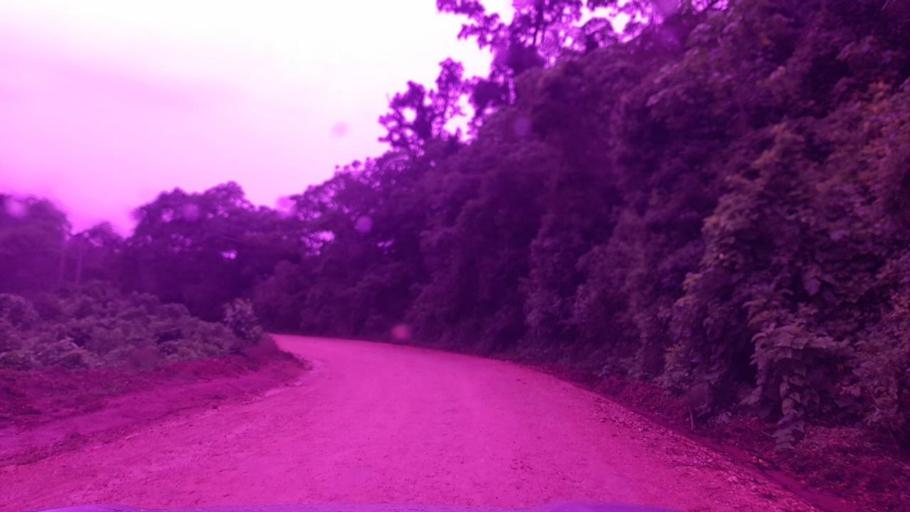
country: ET
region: Southern Nations, Nationalities, and People's Region
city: Bonga
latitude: 7.5066
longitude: 36.0982
